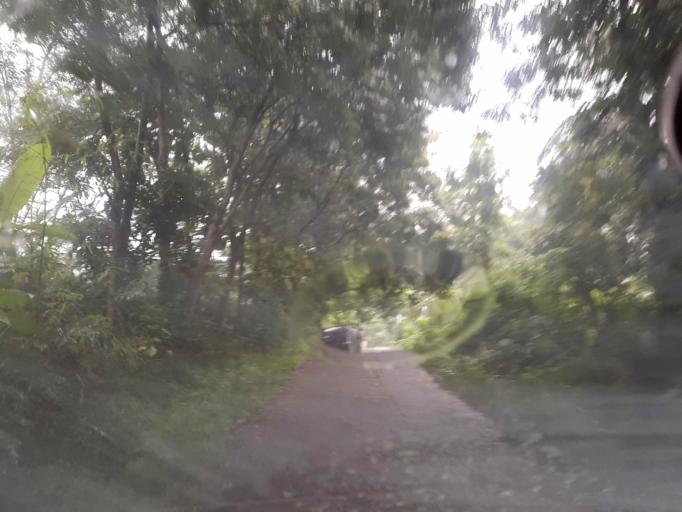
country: ID
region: Central Java
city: Kadumanis
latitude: -7.1783
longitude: 108.9078
